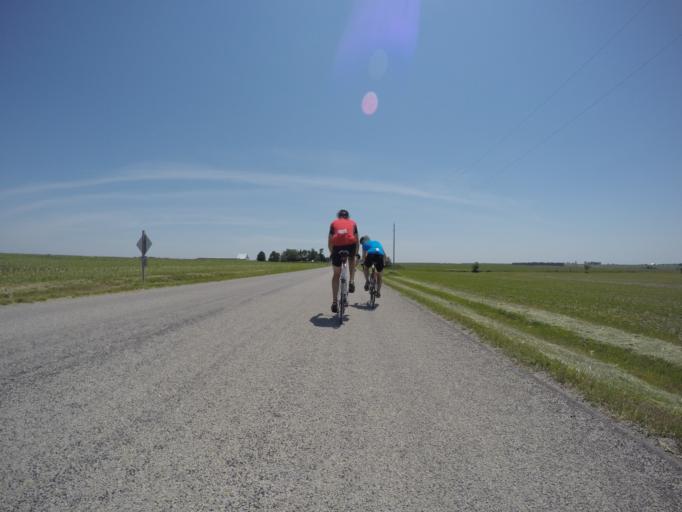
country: US
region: Kansas
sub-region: Nemaha County
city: Sabetha
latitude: 39.9552
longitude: -95.8449
